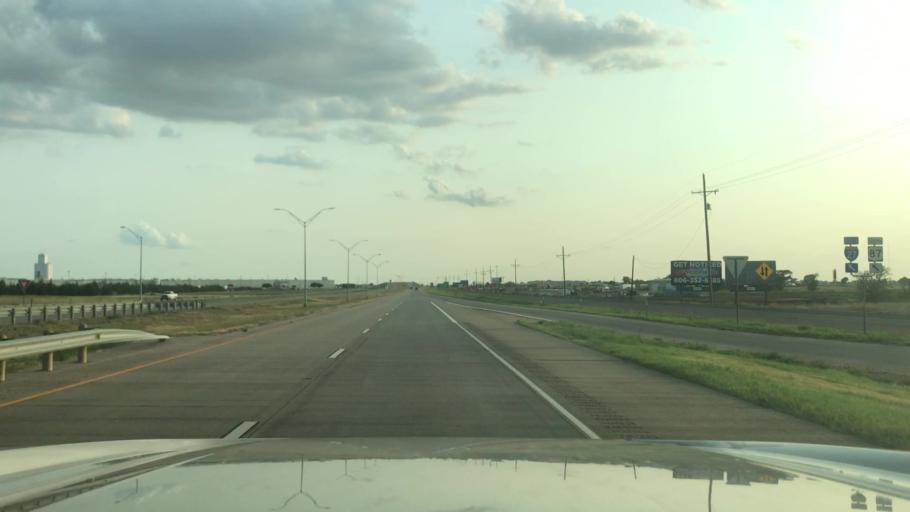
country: US
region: Texas
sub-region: Hale County
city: Seth Ward
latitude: 34.2192
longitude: -101.7257
